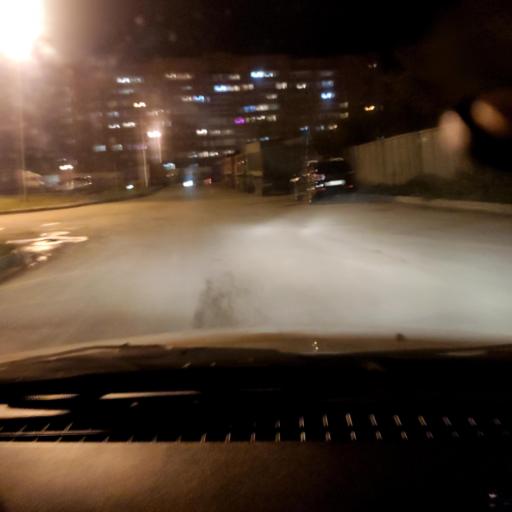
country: RU
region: Bashkortostan
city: Ufa
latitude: 54.7767
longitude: 56.0663
